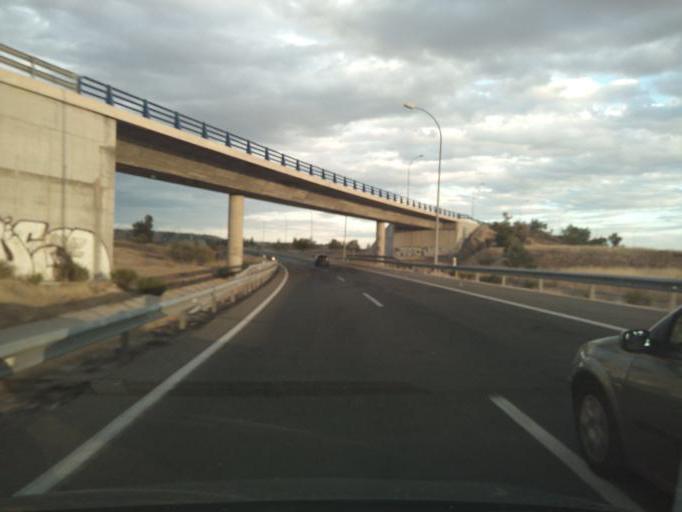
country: ES
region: Madrid
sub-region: Provincia de Madrid
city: San Sebastian de los Reyes
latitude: 40.5449
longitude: -3.5722
